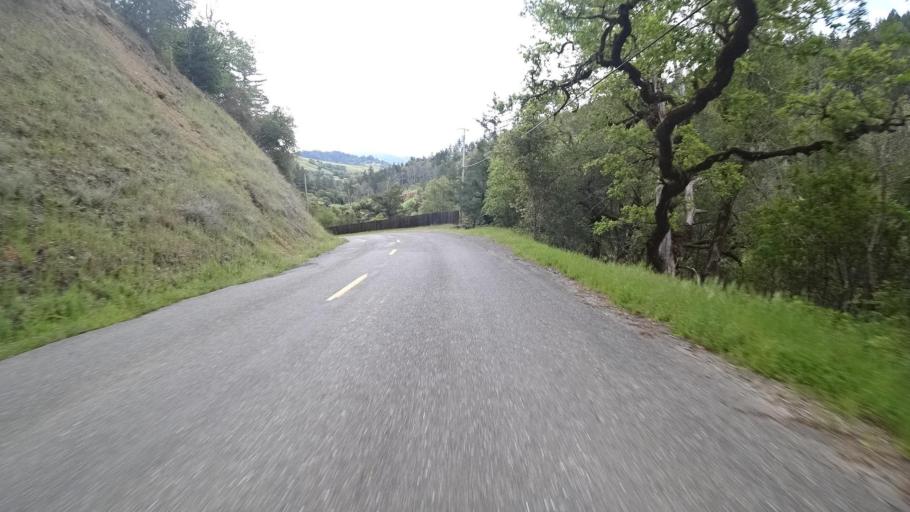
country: US
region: California
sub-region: Humboldt County
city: Redway
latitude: 40.2232
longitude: -123.6046
